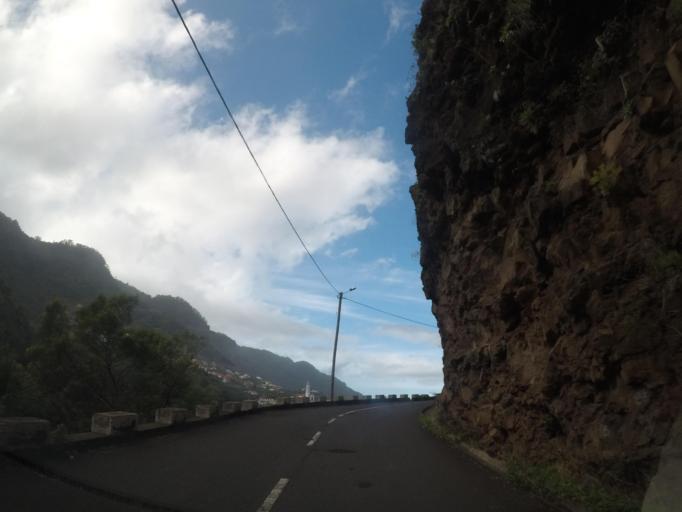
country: PT
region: Madeira
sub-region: Santana
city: Santana
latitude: 32.7847
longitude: -16.8494
